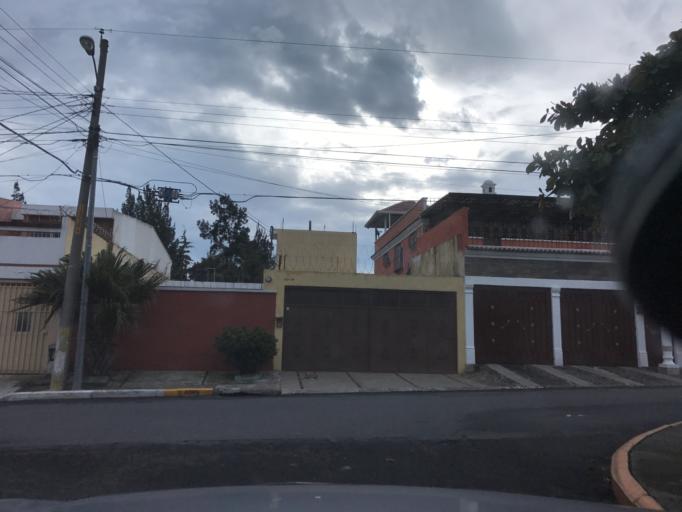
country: GT
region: Guatemala
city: Santa Catarina Pinula
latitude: 14.5768
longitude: -90.5531
